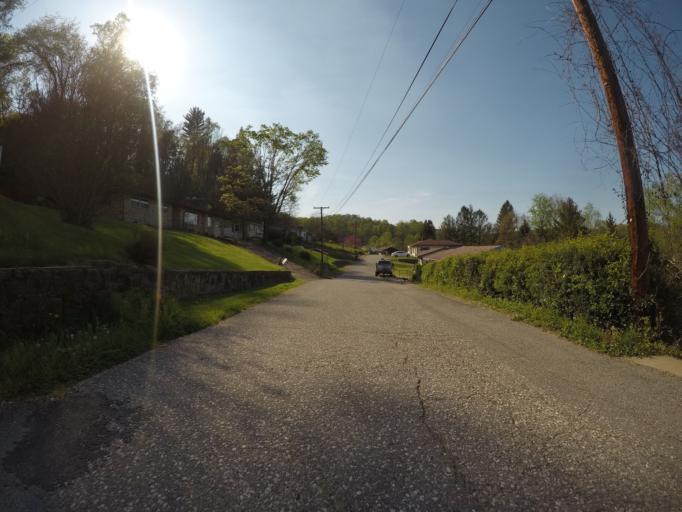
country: US
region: West Virginia
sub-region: Kanawha County
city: Charleston
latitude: 38.3892
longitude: -81.6012
